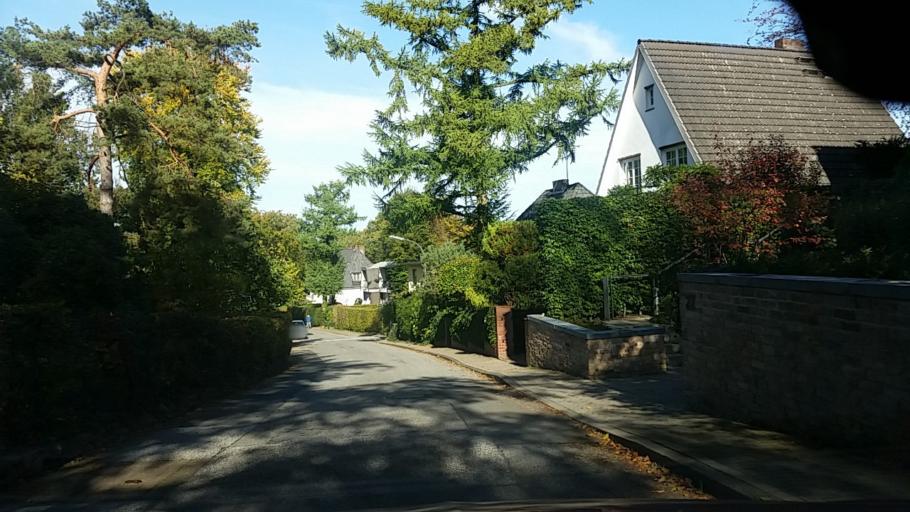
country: DE
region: Schleswig-Holstein
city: Halstenbek
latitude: 53.5677
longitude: 9.8044
